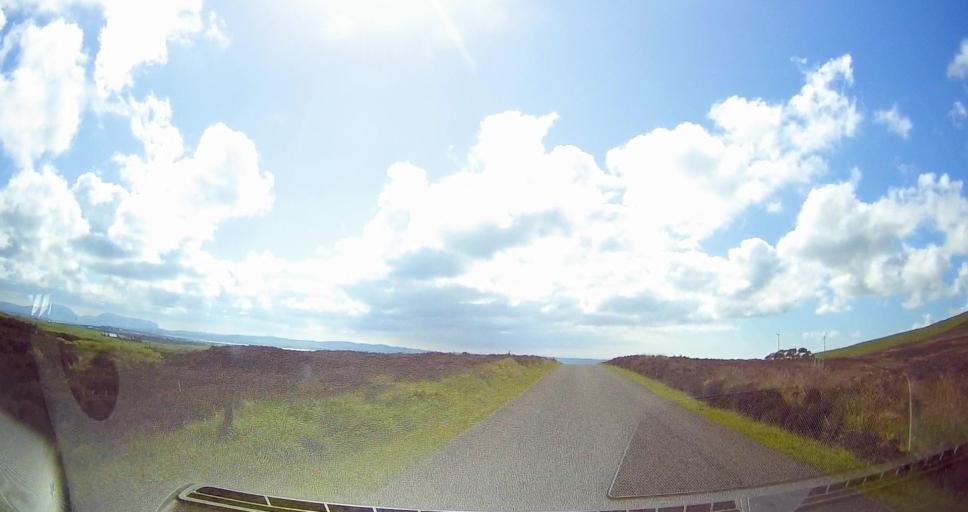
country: GB
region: Scotland
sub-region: Orkney Islands
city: Stromness
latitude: 59.0469
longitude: -3.1394
